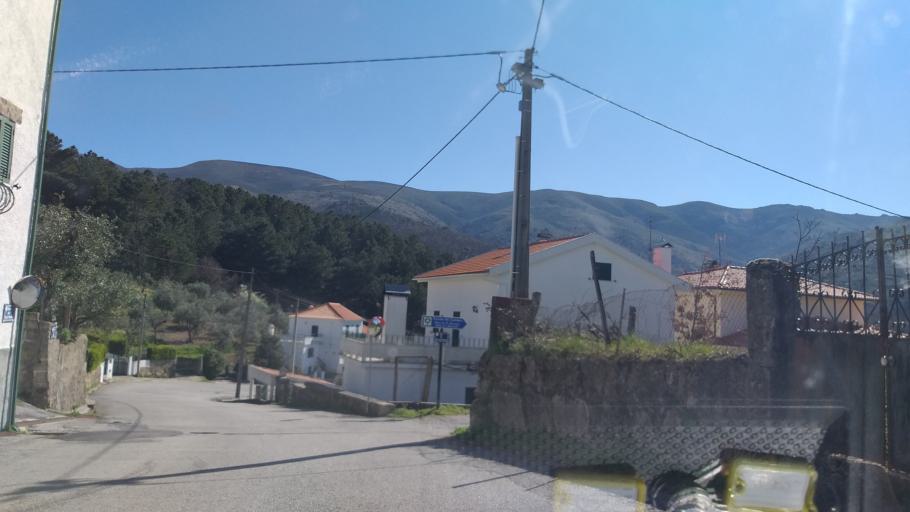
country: PT
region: Guarda
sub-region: Manteigas
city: Manteigas
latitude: 40.4730
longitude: -7.6020
